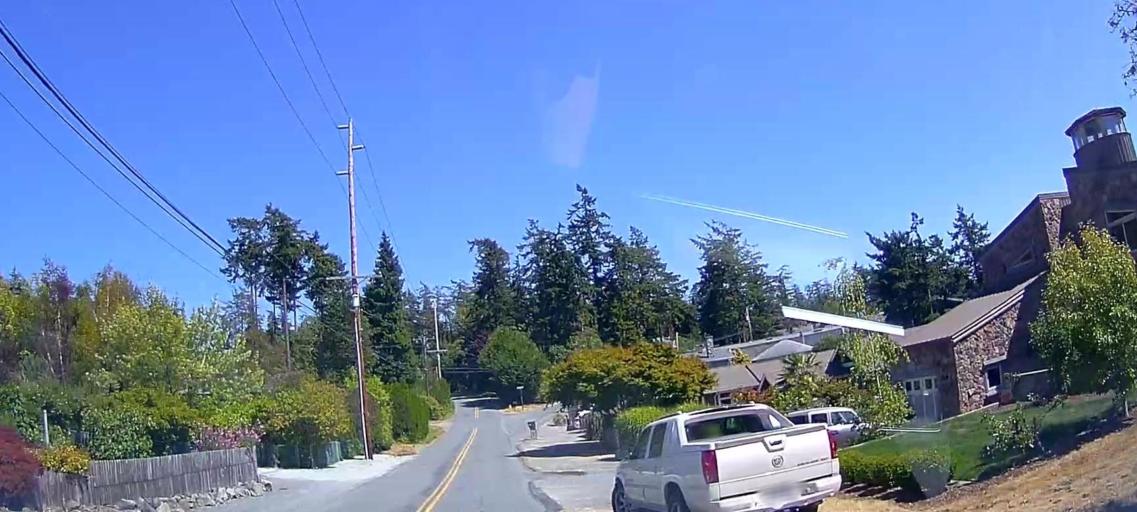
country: US
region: Washington
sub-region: Skagit County
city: Anacortes
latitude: 48.4479
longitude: -122.5709
